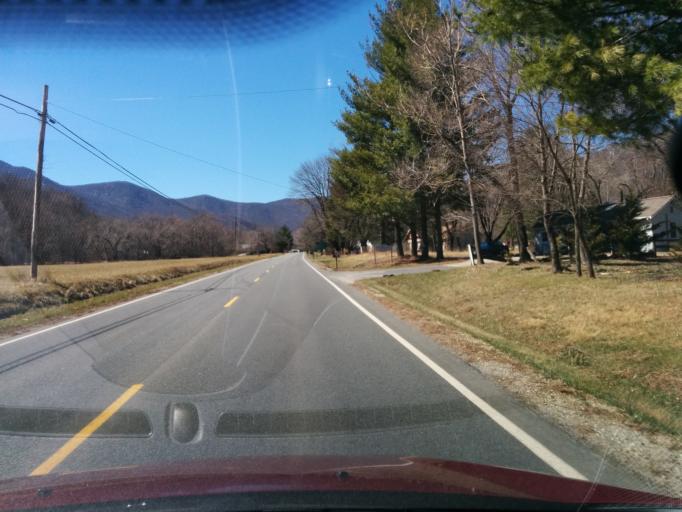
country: US
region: Virginia
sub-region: Nelson County
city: Nellysford
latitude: 37.8737
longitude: -78.9287
